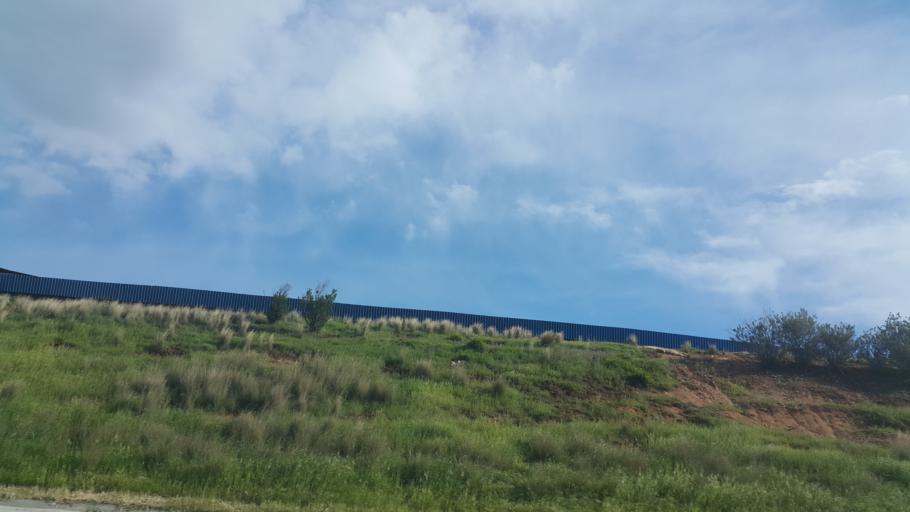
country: TR
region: Adana
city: Yakapinar
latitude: 36.9898
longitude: 35.6125
